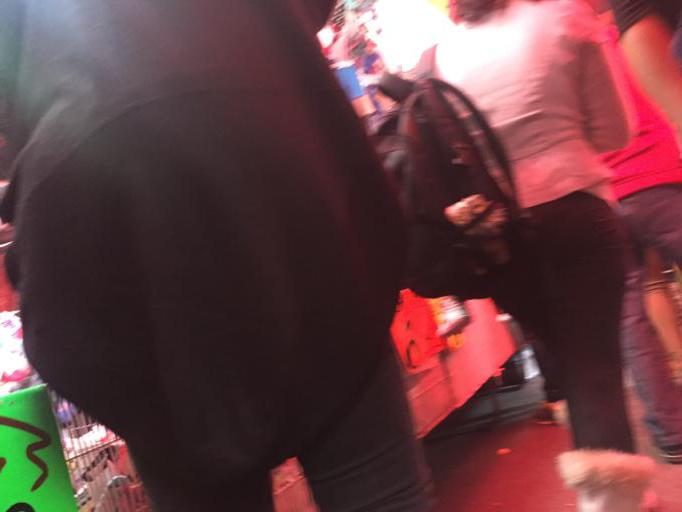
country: MX
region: Mexico
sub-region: Tlalnepantla de Baz
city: Puerto Escondido (Tepeolulco Puerto Escondido)
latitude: 19.5649
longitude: -99.0875
